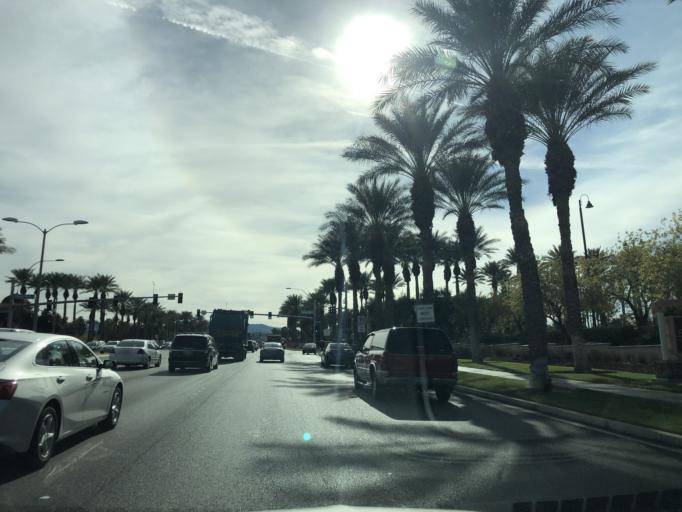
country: US
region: Nevada
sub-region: Clark County
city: Whitney
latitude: 36.0231
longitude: -115.0845
